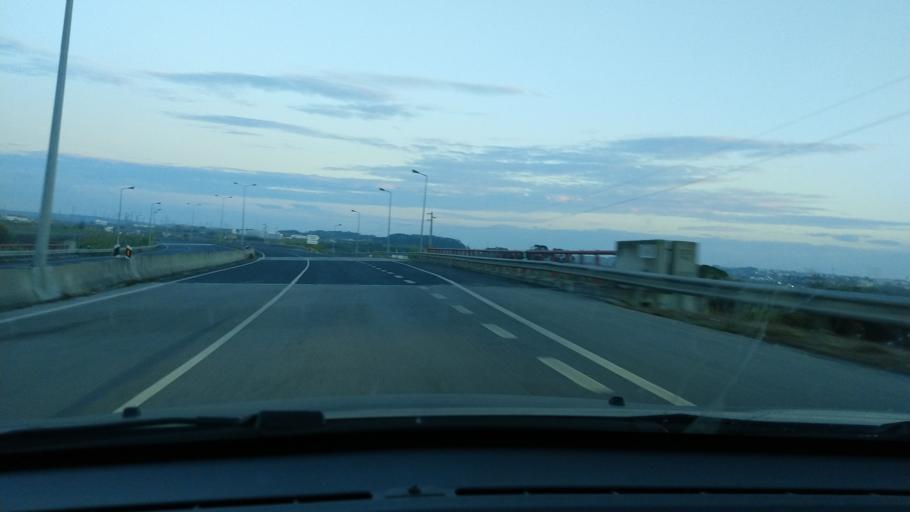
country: PT
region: Leiria
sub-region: Peniche
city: Atouguia da Baleia
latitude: 39.3318
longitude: -9.3332
